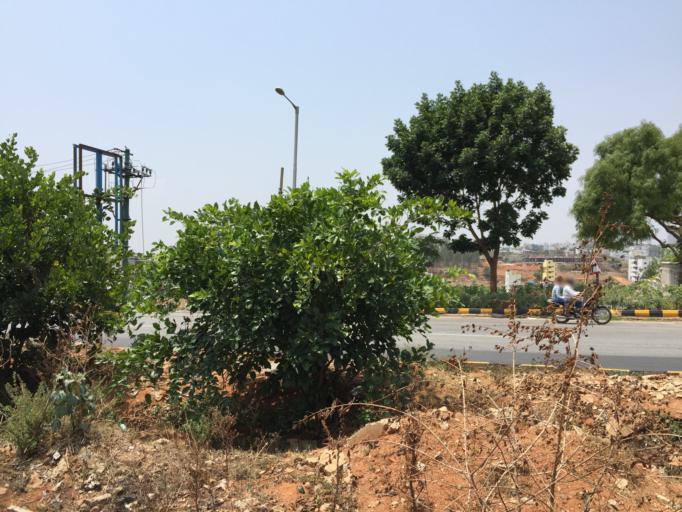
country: IN
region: Karnataka
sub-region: Bangalore Urban
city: Bangalore
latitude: 12.8928
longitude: 77.5288
